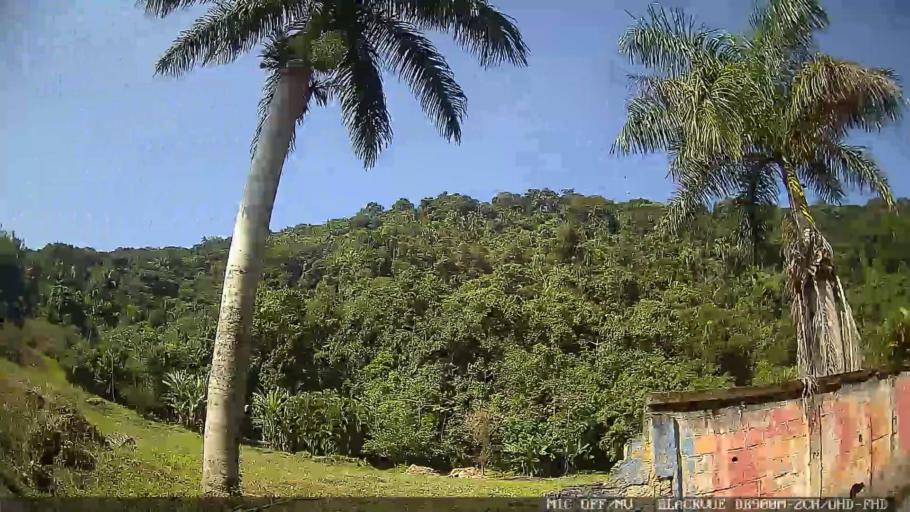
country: BR
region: Sao Paulo
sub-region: Guaruja
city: Guaruja
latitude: -24.0091
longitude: -46.2898
